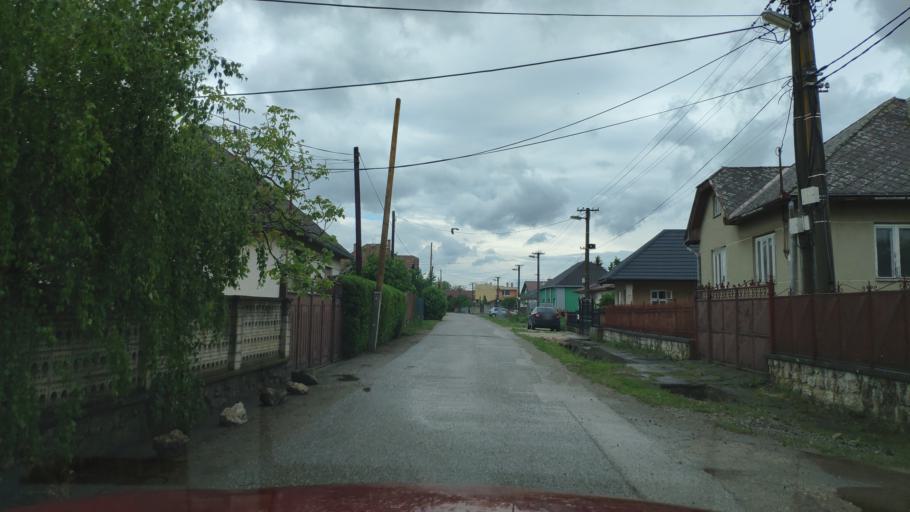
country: SK
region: Kosicky
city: Moldava nad Bodvou
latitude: 48.5708
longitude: 21.1217
